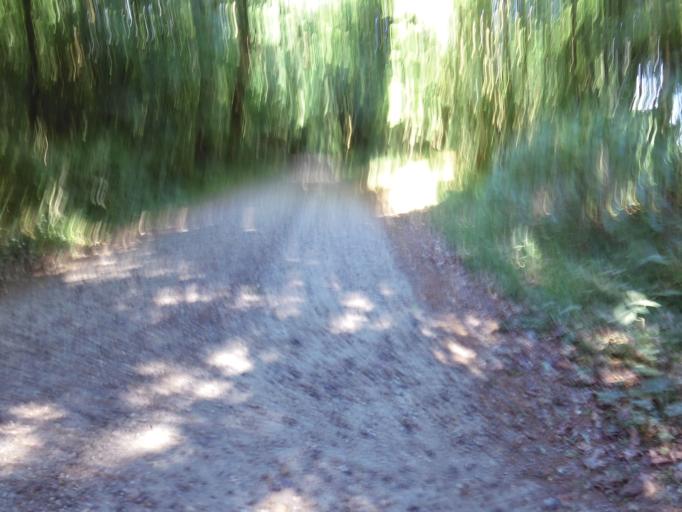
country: DK
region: Central Jutland
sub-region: Holstebro Kommune
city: Vinderup
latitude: 56.4476
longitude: 8.8257
